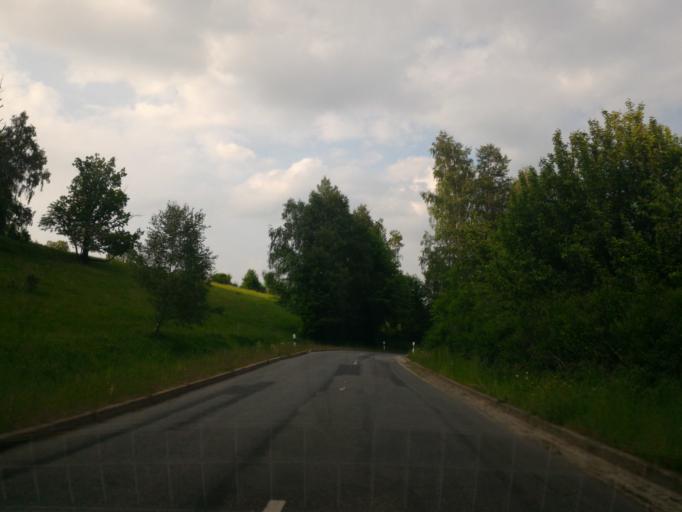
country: DE
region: Saxony
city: Grossschonau
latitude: 50.8646
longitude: 14.6607
